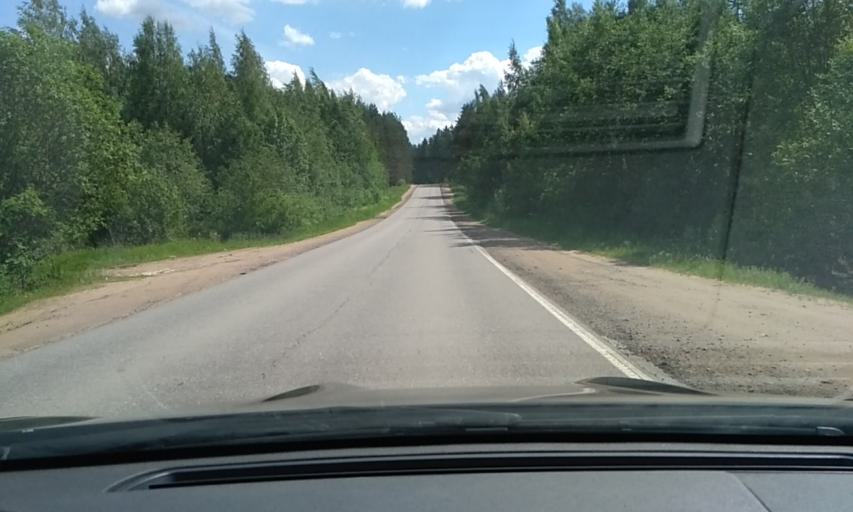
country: RU
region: Leningrad
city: Imeni Sverdlova
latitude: 59.8444
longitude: 30.6880
